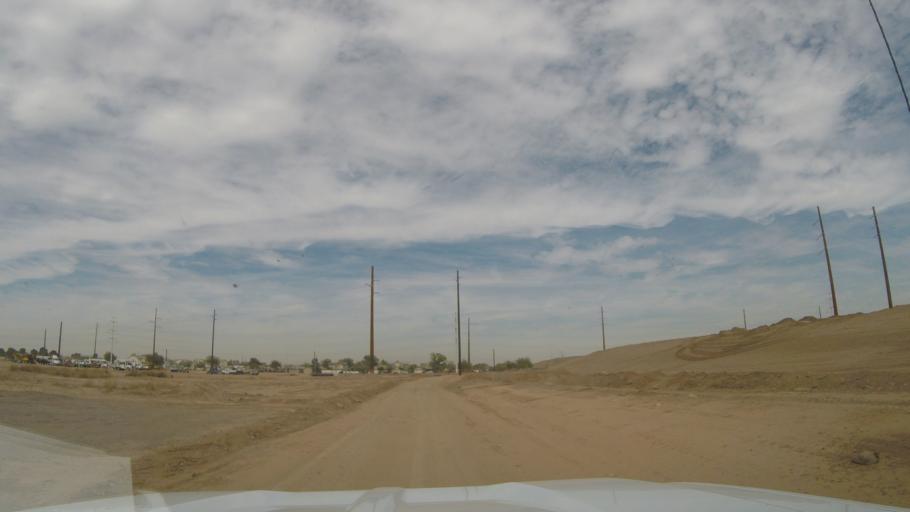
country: US
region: Arizona
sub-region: Maricopa County
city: Laveen
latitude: 33.4059
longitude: -112.1927
